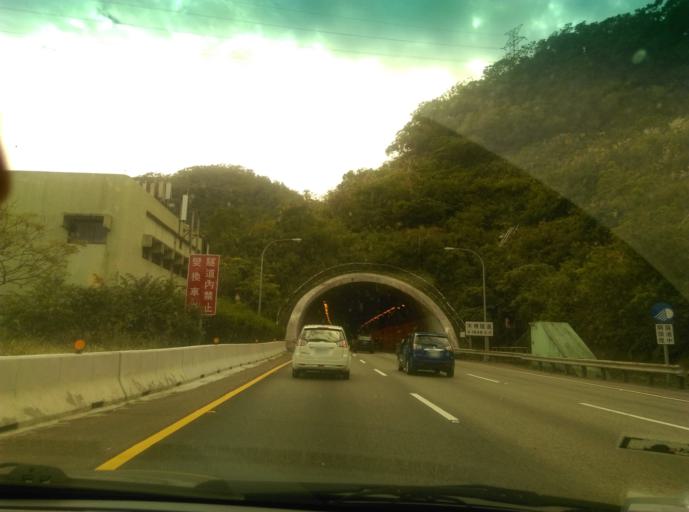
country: TW
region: Taipei
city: Taipei
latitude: 24.9929
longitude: 121.5928
